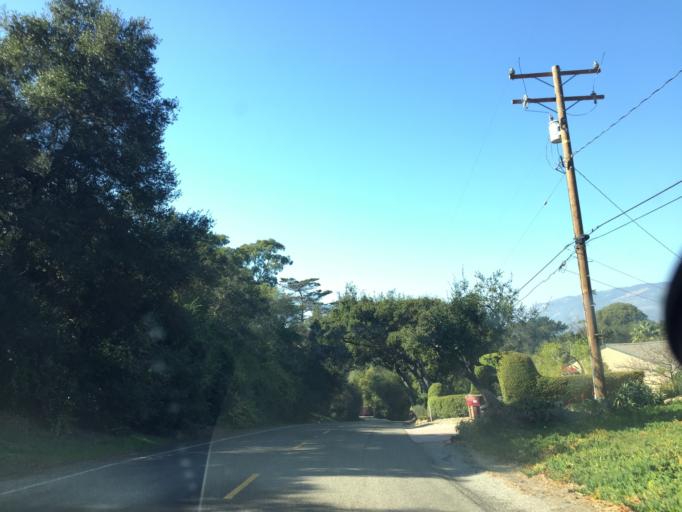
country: US
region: California
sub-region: Santa Barbara County
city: Mission Canyon
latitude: 34.4327
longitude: -119.7662
